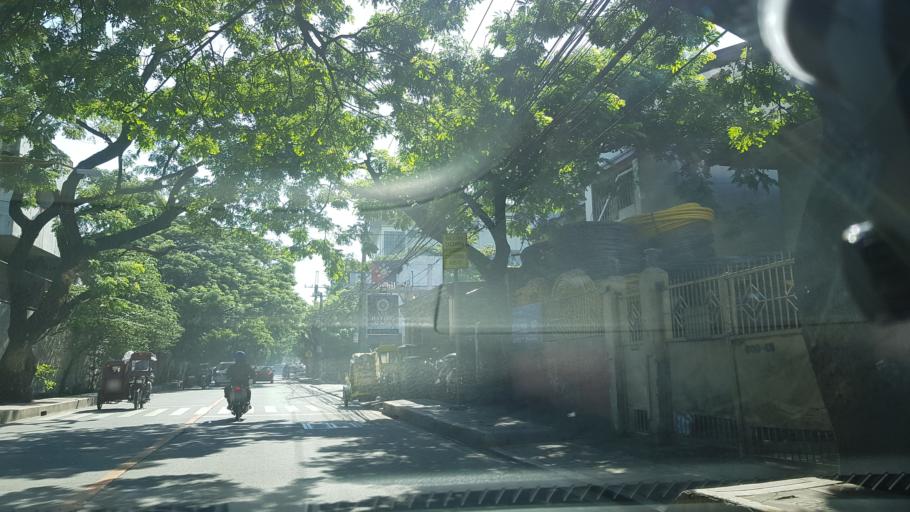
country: PH
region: Calabarzon
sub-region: Province of Rizal
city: Cainta
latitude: 14.5754
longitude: 121.0954
